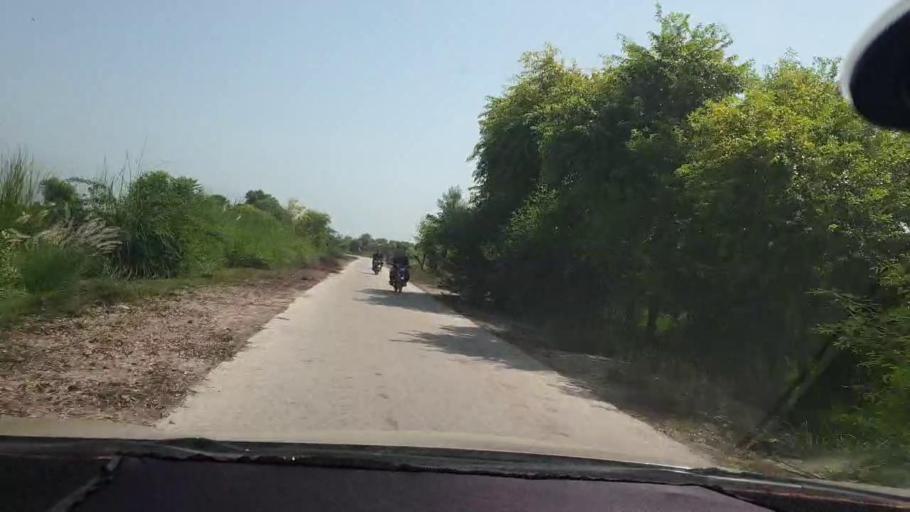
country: PK
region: Sindh
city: Kambar
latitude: 27.5116
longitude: 68.0118
